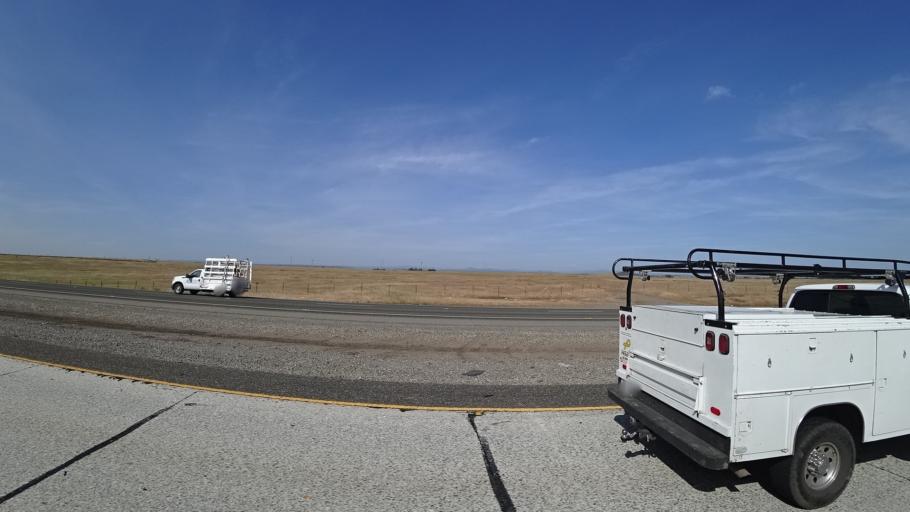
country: US
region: California
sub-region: Butte County
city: Durham
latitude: 39.6711
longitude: -121.7511
